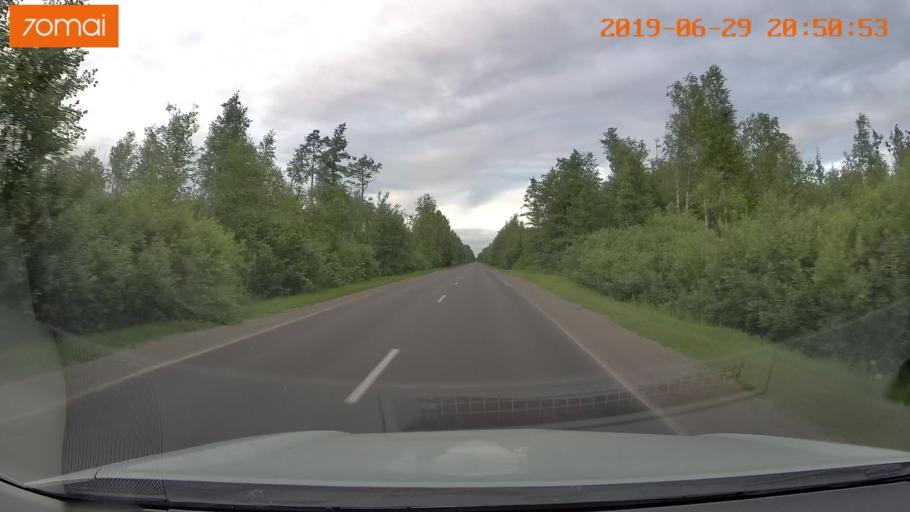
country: BY
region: Brest
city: Hantsavichy
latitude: 52.6816
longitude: 26.3419
